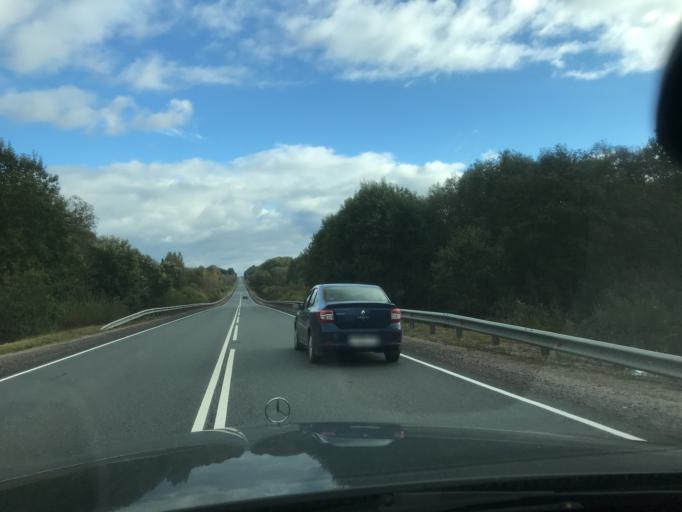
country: RU
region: Pskov
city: Opochka
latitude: 56.6534
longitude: 28.7615
